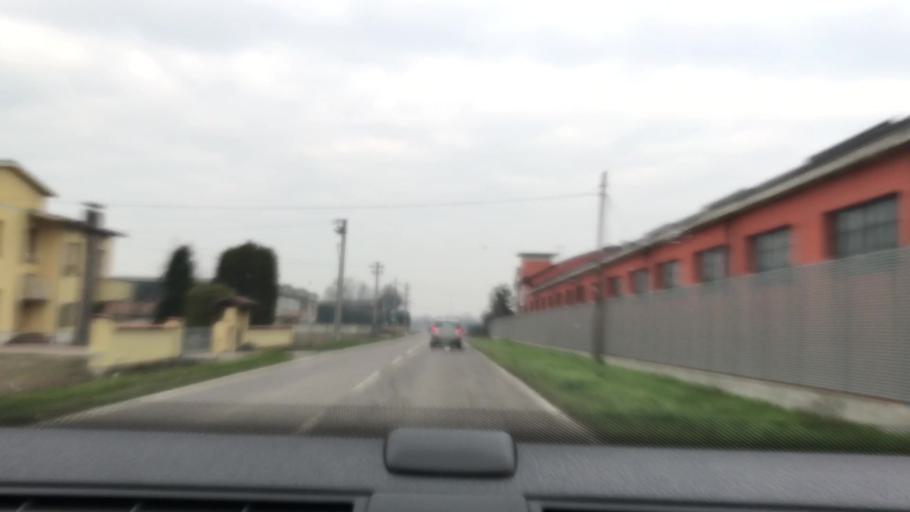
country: IT
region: Lombardy
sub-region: Provincia di Mantova
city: Dosolo
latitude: 44.9438
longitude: 10.6268
